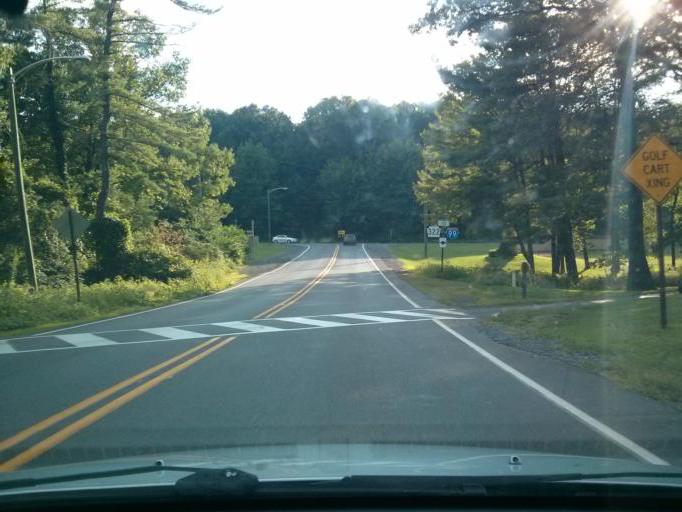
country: US
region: Pennsylvania
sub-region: Centre County
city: Park Forest Village
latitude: 40.8220
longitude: -77.9005
